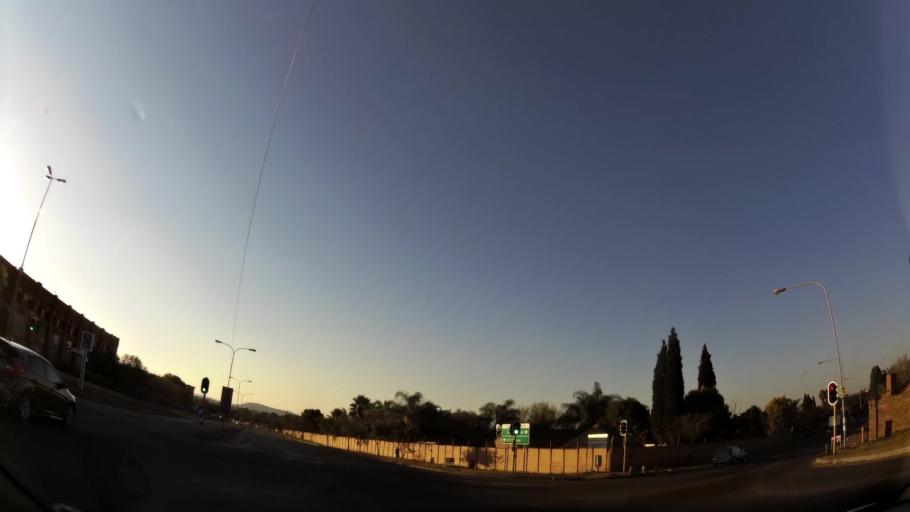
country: ZA
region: Gauteng
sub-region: City of Tshwane Metropolitan Municipality
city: Centurion
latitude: -25.8733
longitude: 28.1393
